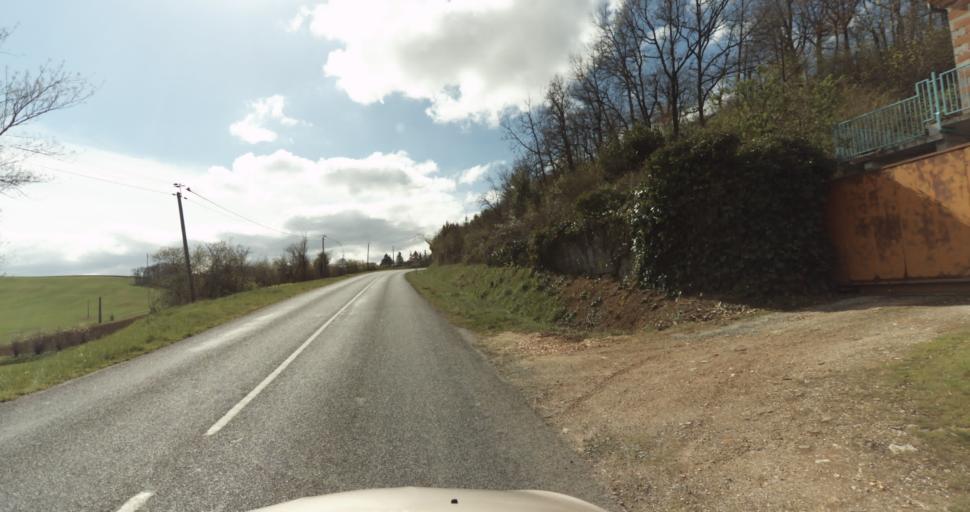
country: FR
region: Midi-Pyrenees
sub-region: Departement du Tarn
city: Puygouzon
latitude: 43.8833
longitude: 2.1551
